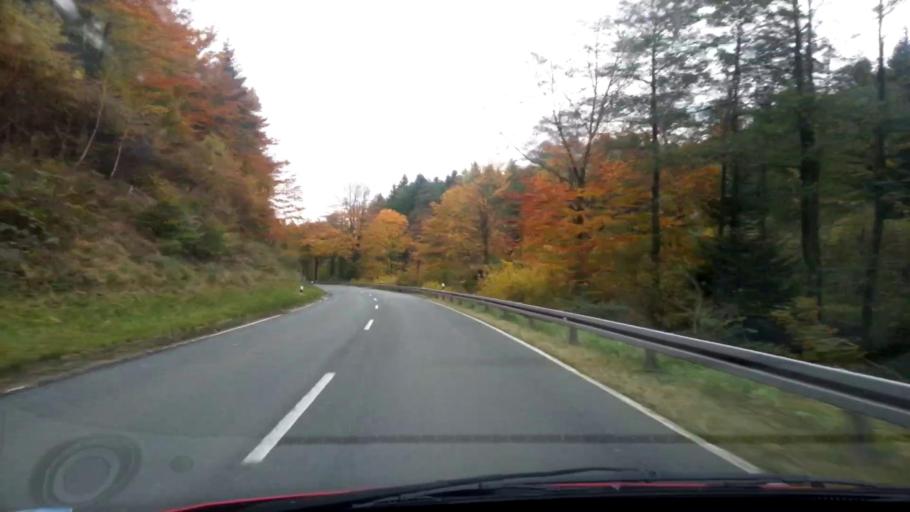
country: DE
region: Bavaria
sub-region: Upper Franconia
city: Kirchenpingarten
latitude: 49.9555
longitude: 11.7601
